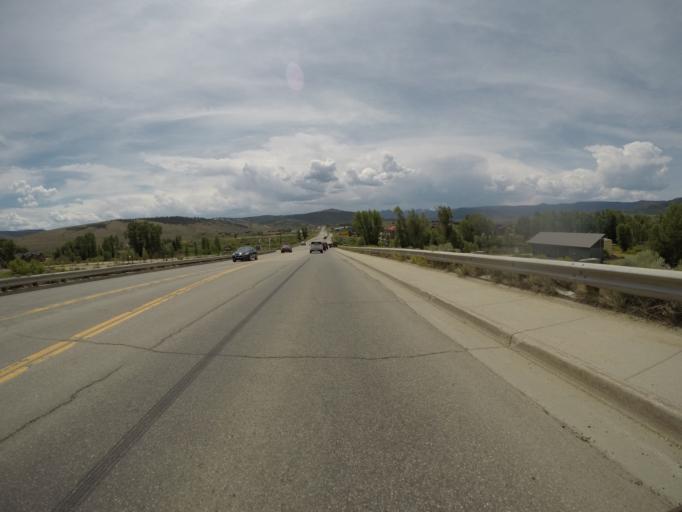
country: US
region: Colorado
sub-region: Grand County
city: Granby
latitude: 40.0829
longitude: -105.9299
